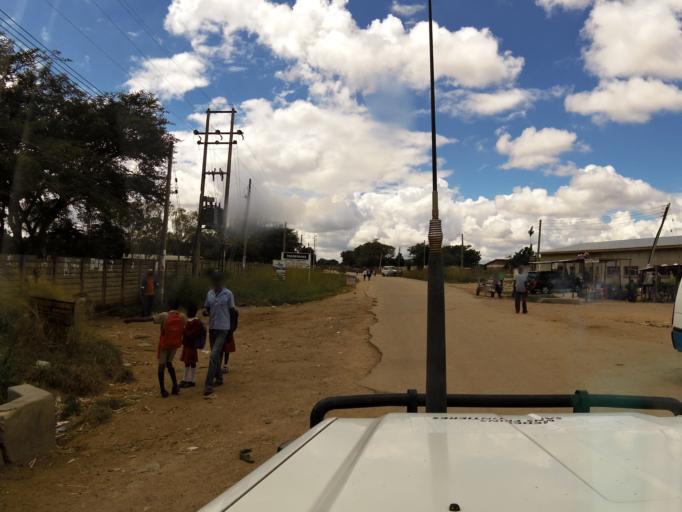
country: ZW
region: Harare
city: Epworth
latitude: -17.9088
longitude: 31.1623
